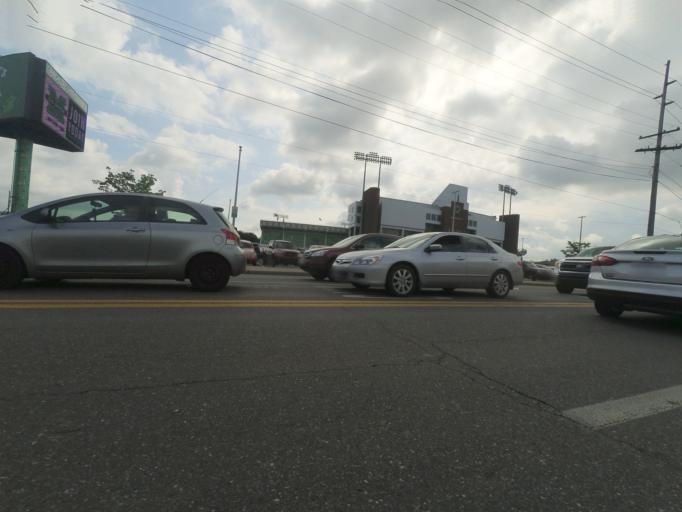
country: US
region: West Virginia
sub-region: Cabell County
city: Huntington
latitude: 38.4253
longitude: -82.4233
